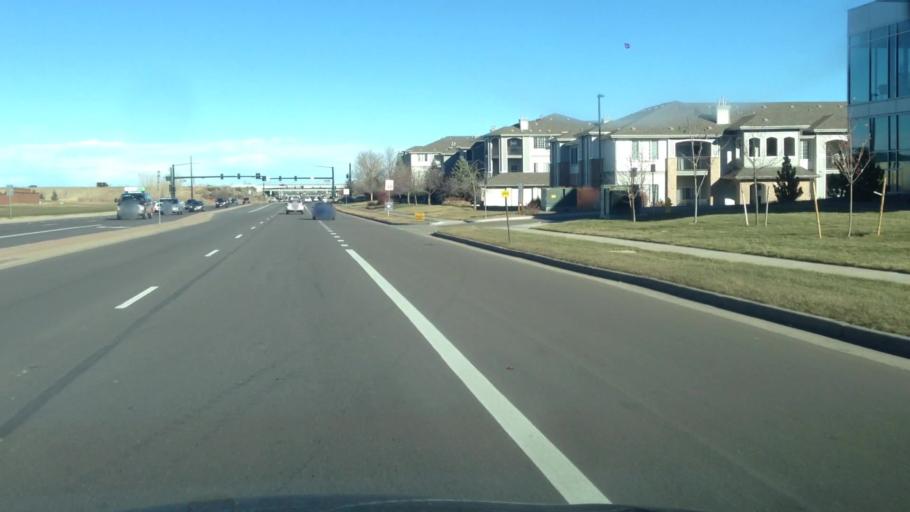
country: US
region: Colorado
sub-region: Douglas County
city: Stonegate
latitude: 39.5437
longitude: -104.7934
